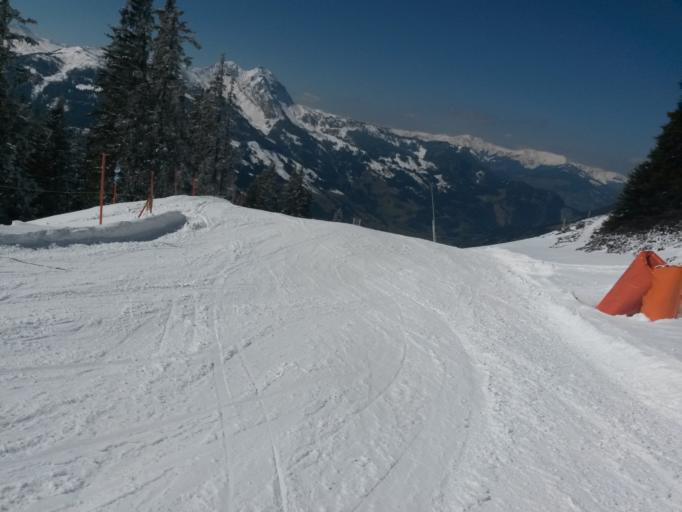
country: AT
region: Salzburg
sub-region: Politischer Bezirk Sankt Johann im Pongau
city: Dorfgastein
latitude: 47.2346
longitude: 13.1441
